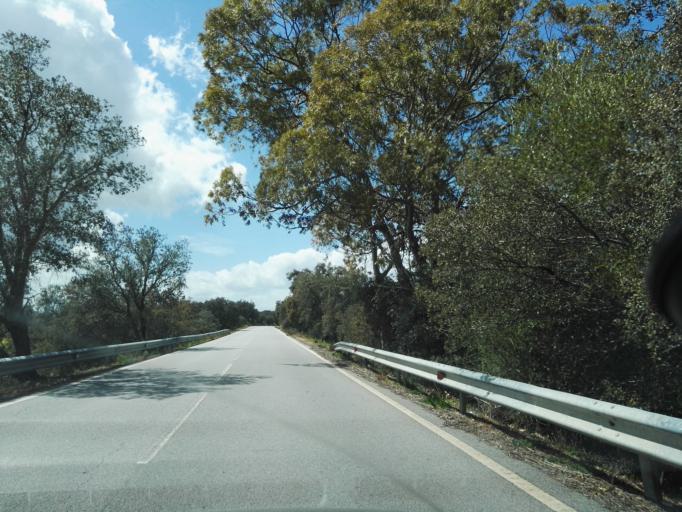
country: PT
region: Portalegre
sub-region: Campo Maior
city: Campo Maior
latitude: 38.9945
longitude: -7.1518
